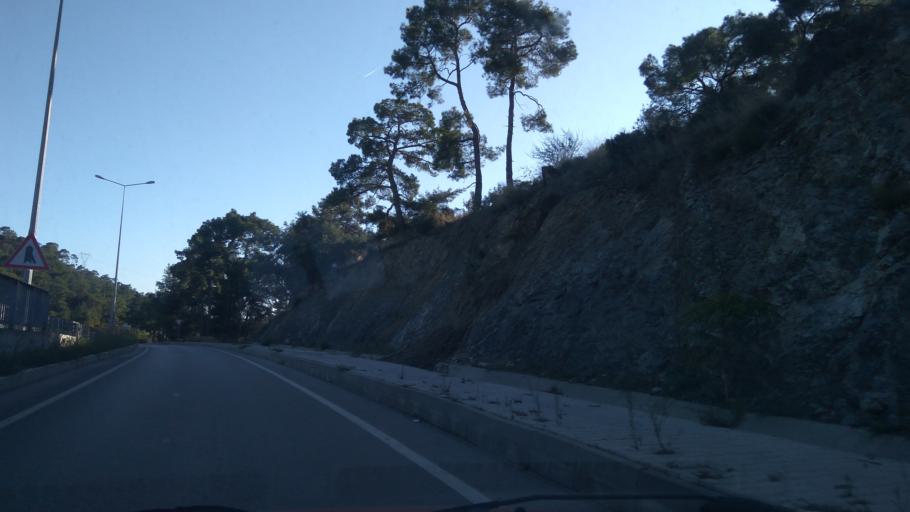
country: TR
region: Antalya
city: Kemer
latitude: 36.5895
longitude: 30.5409
